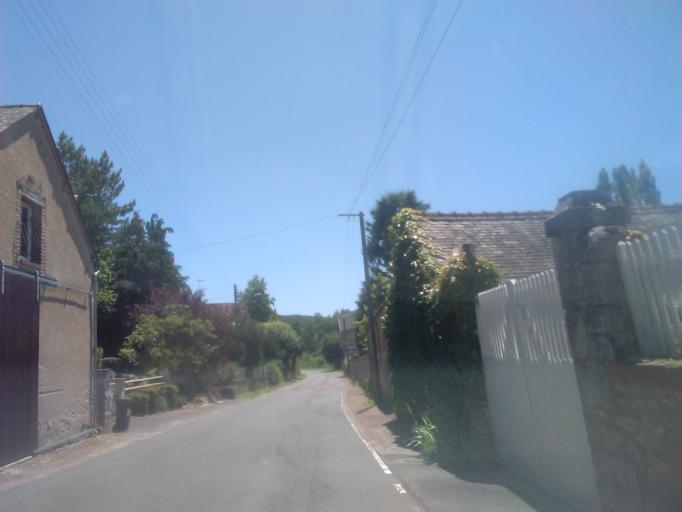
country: FR
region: Centre
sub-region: Departement du Loir-et-Cher
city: Saint-Sulpice-de-Pommeray
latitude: 47.5758
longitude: 1.2182
